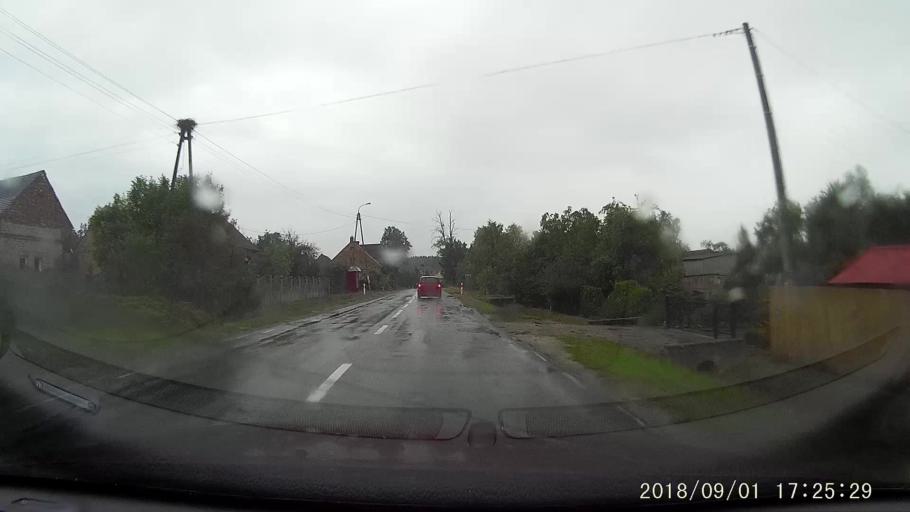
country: PL
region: Lubusz
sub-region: Powiat zaganski
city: Zagan
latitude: 51.6859
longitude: 15.3087
